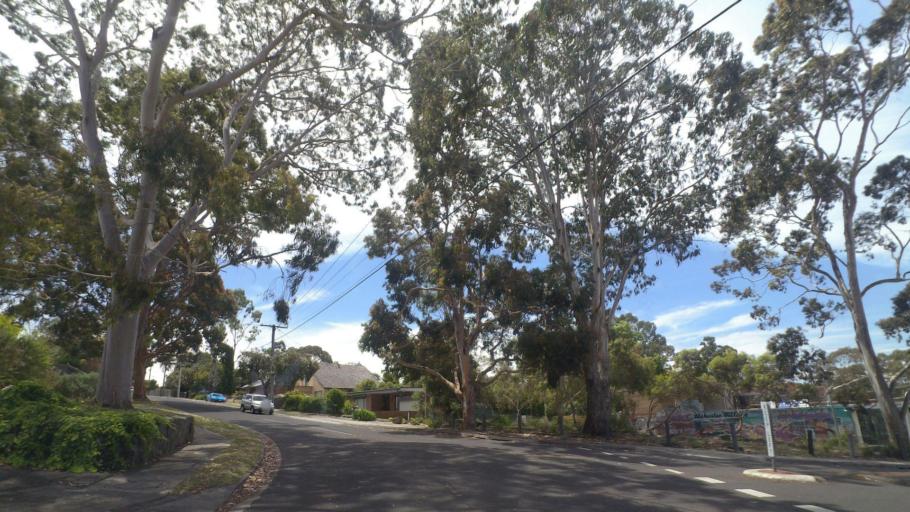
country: AU
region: Victoria
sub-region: Maroondah
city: Bayswater North
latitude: -37.8448
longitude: 145.2985
